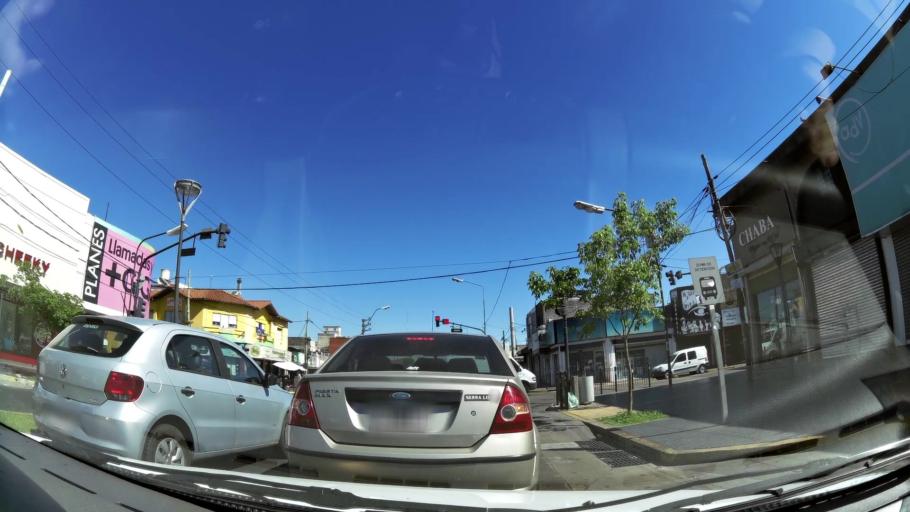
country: AR
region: Buenos Aires
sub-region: Partido de Vicente Lopez
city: Olivos
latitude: -34.5274
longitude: -58.5178
